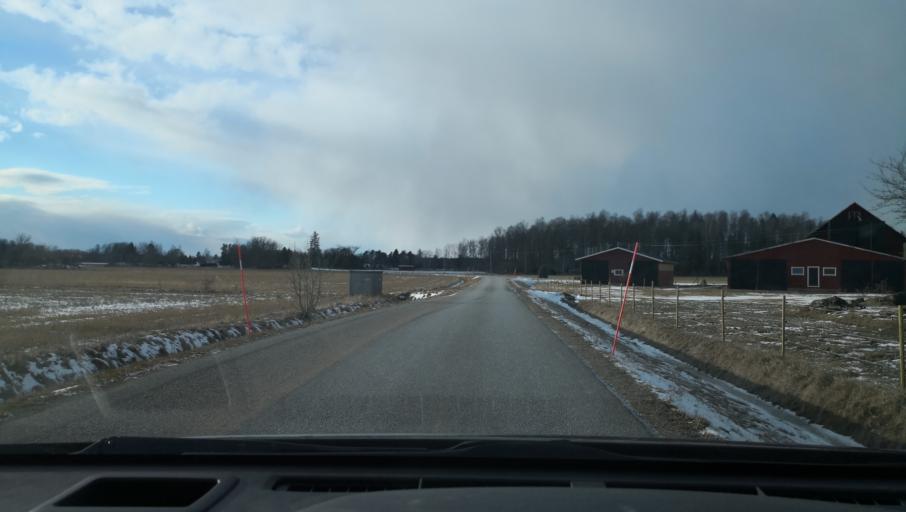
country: SE
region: Uppsala
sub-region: Enkopings Kommun
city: Irsta
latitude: 59.7013
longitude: 16.9400
